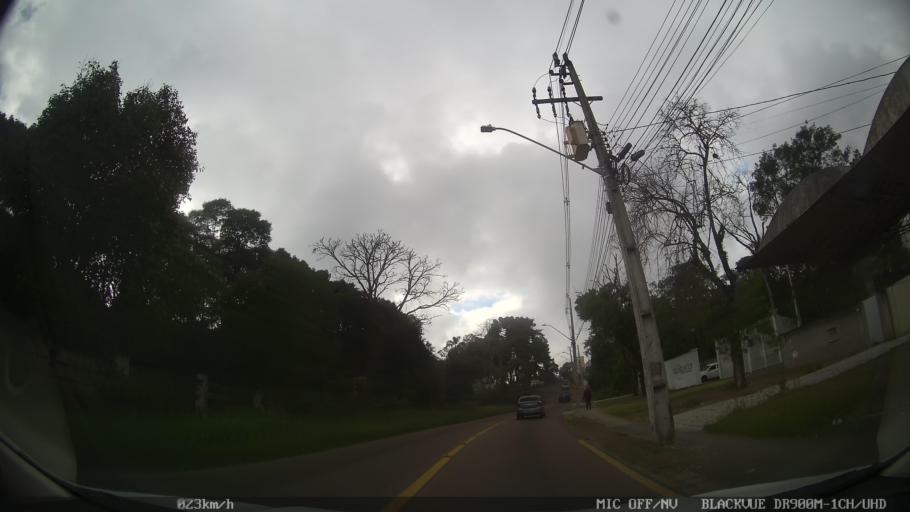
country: BR
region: Parana
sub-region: Almirante Tamandare
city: Almirante Tamandare
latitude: -25.3605
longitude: -49.2505
